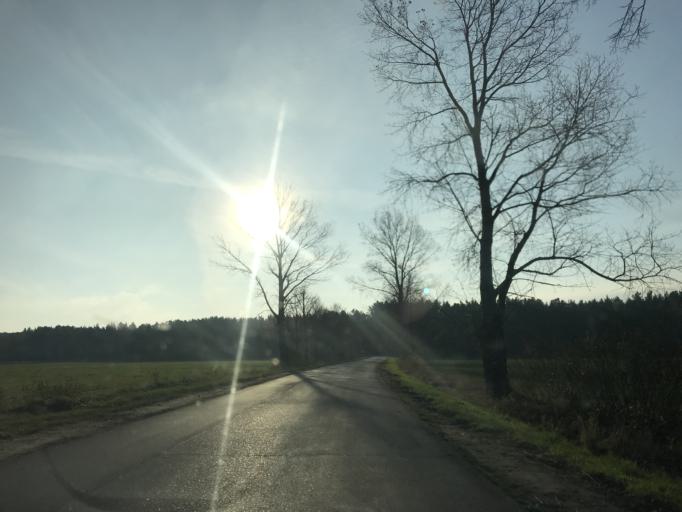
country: PL
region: Pomeranian Voivodeship
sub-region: Powiat pucki
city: Krokowa
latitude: 54.8064
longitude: 18.0988
